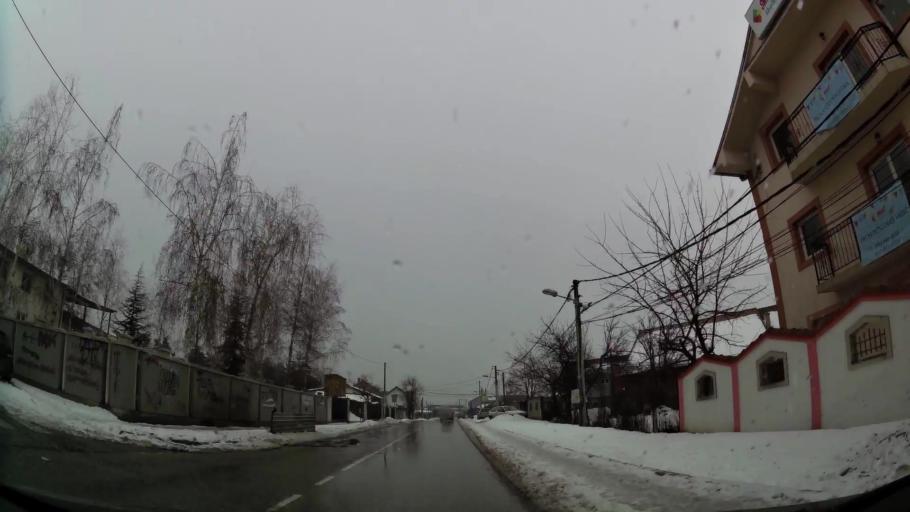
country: RS
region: Central Serbia
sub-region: Belgrade
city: Zemun
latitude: 44.8479
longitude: 20.3553
